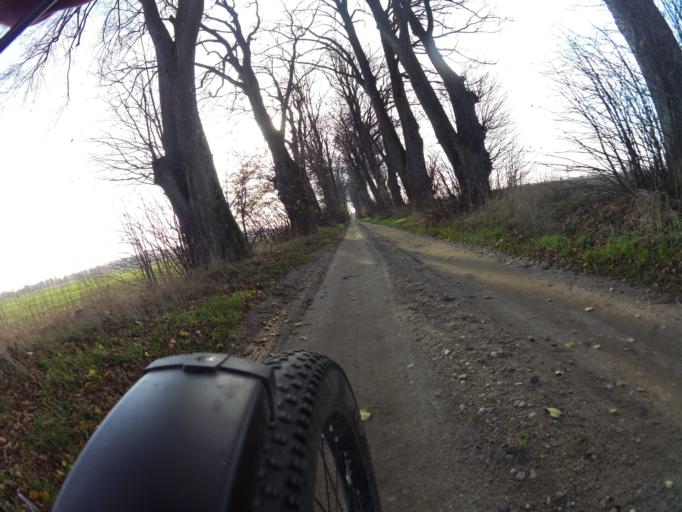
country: PL
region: Pomeranian Voivodeship
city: Strzelno
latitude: 54.7525
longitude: 18.2904
